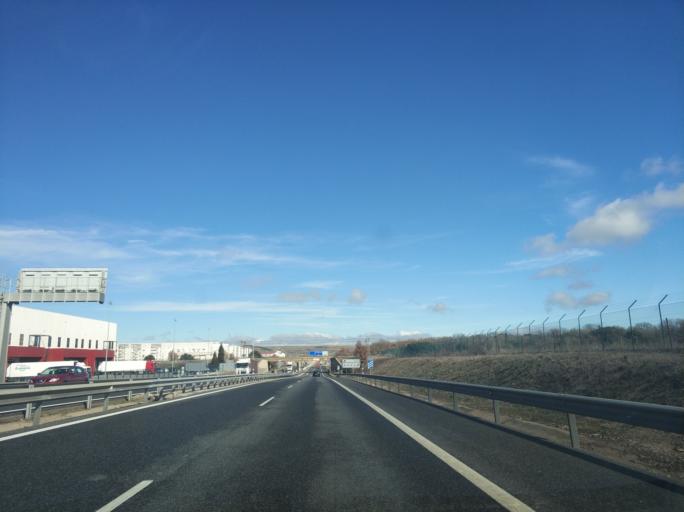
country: ES
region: Castille and Leon
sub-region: Provincia de Burgos
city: Cardenajimeno
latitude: 42.3542
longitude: -3.6374
